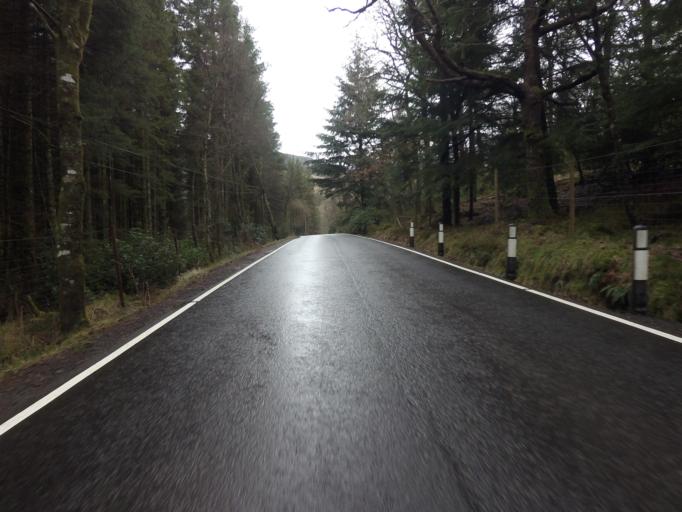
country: GB
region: Scotland
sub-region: Stirling
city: Balfron
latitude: 56.1832
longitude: -4.4451
